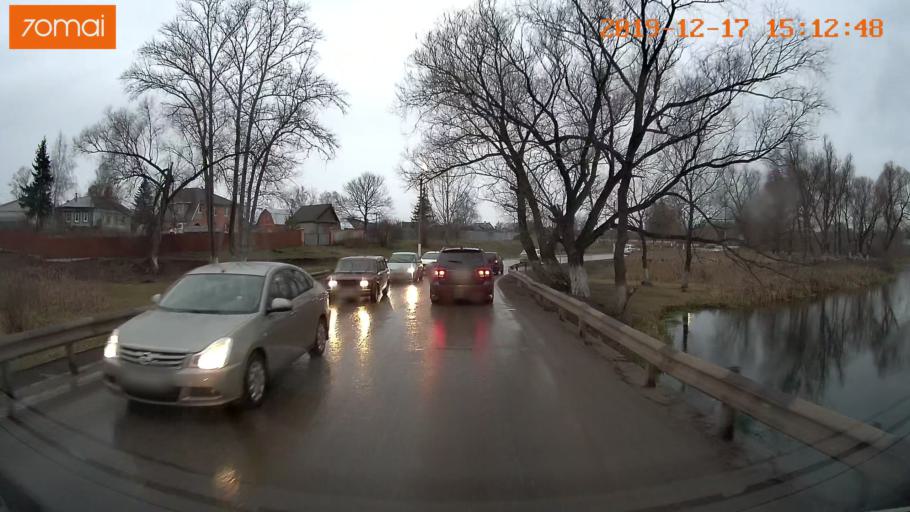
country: RU
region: Rjazan
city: Mikhaylov
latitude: 54.2344
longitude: 39.0233
